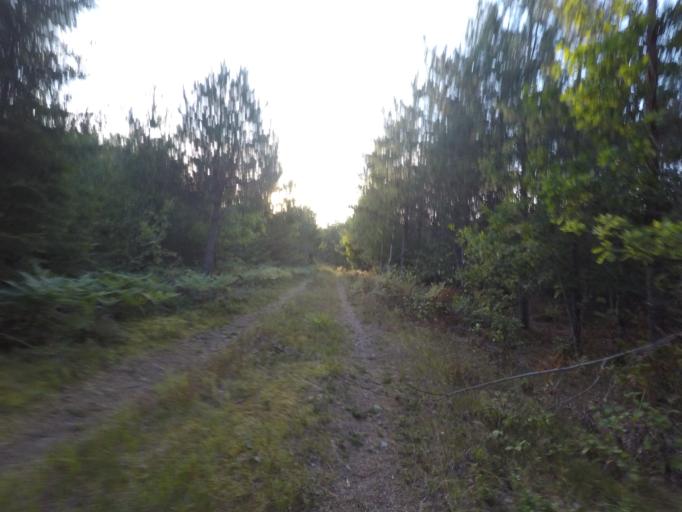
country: SE
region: Soedermanland
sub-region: Eskilstuna Kommun
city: Kvicksund
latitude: 59.4202
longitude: 16.3170
